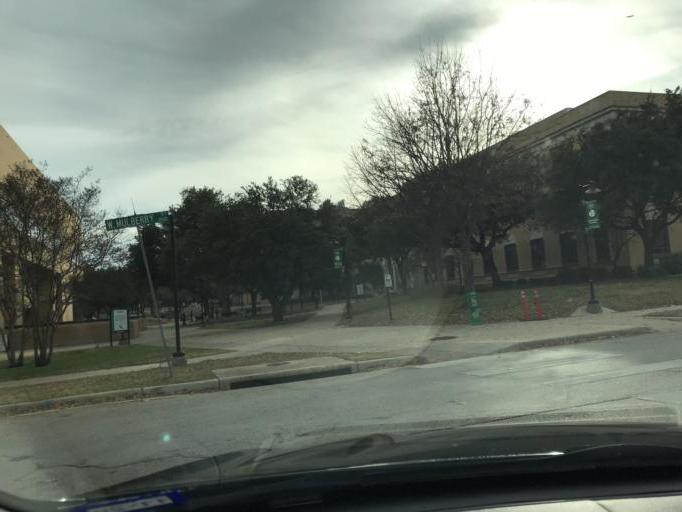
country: US
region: Texas
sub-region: Denton County
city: Denton
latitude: 33.2137
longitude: -97.1485
